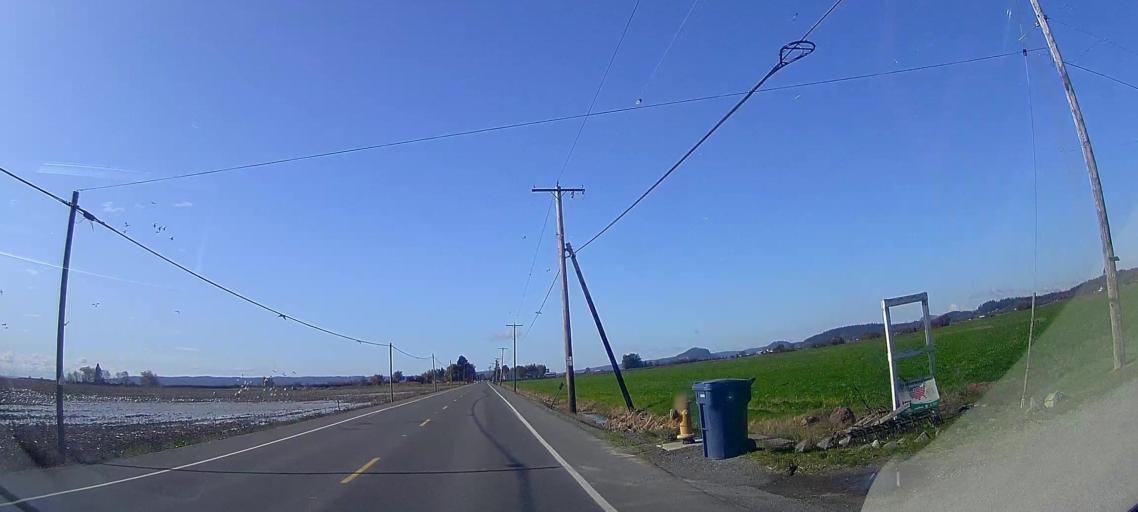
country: US
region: Washington
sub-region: Snohomish County
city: Stanwood
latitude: 48.3413
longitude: -122.4046
